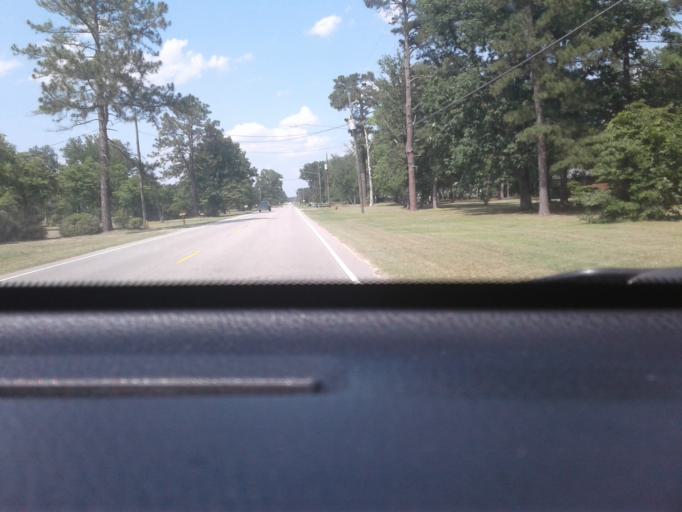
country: US
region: North Carolina
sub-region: Cumberland County
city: Eastover
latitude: 35.1501
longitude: -78.7379
